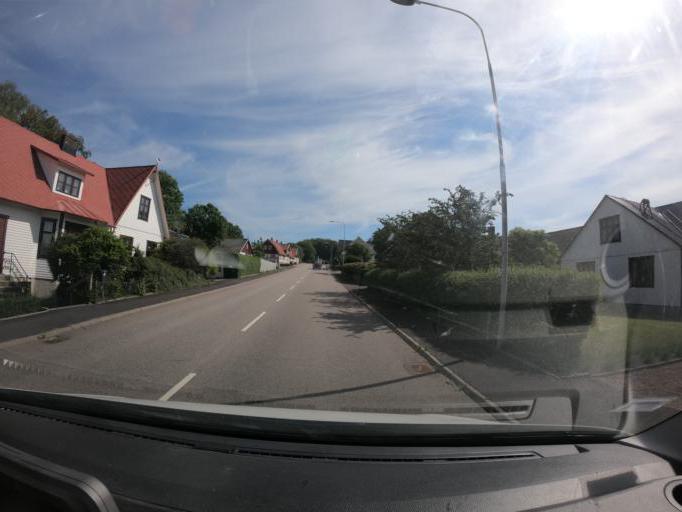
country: SE
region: Skane
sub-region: Bastads Kommun
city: Forslov
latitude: 56.4104
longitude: 12.7445
